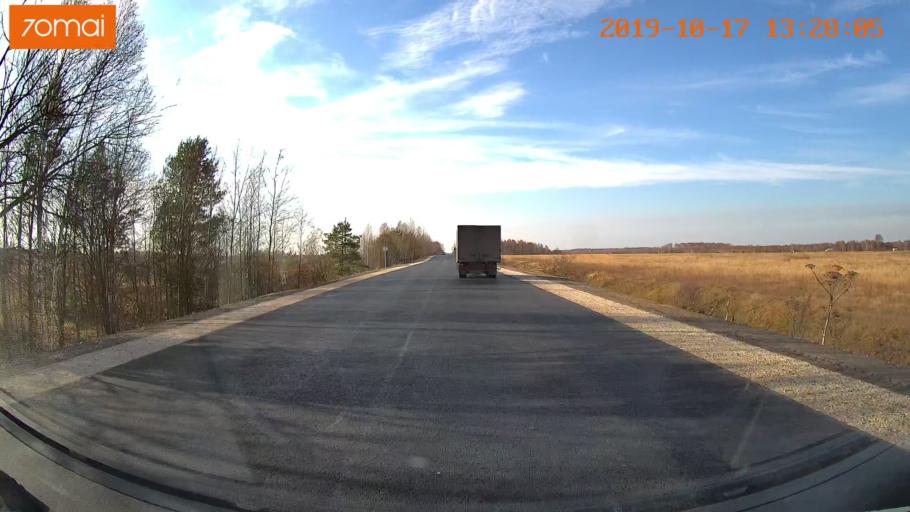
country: RU
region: Vladimir
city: Velikodvorskiy
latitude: 55.1151
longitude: 40.8784
